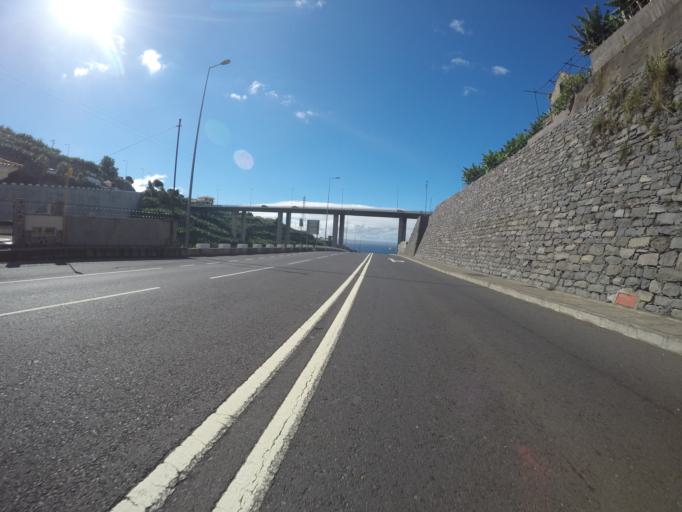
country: PT
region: Madeira
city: Camara de Lobos
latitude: 32.6530
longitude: -16.9598
